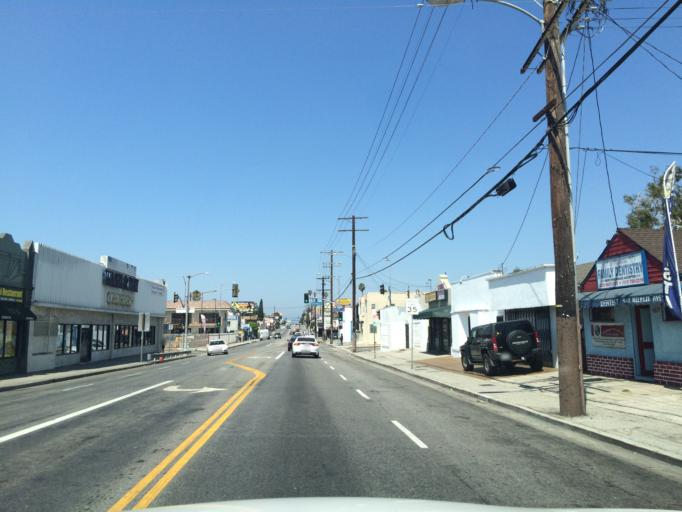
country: US
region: California
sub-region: Los Angeles County
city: Hollywood
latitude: 34.0836
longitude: -118.3008
